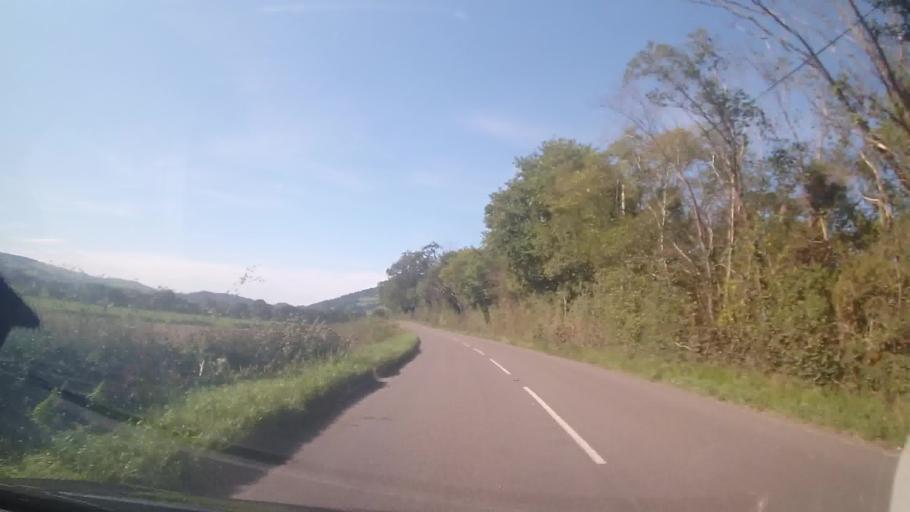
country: GB
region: Wales
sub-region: Sir Powys
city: Montgomery
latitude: 52.5298
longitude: -3.1275
